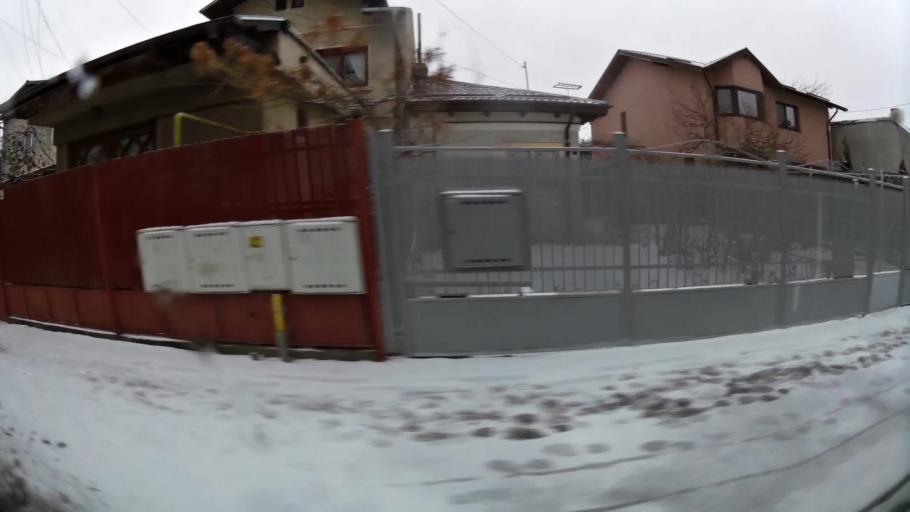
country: RO
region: Prahova
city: Ploiesti
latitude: 44.9339
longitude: 26.0421
